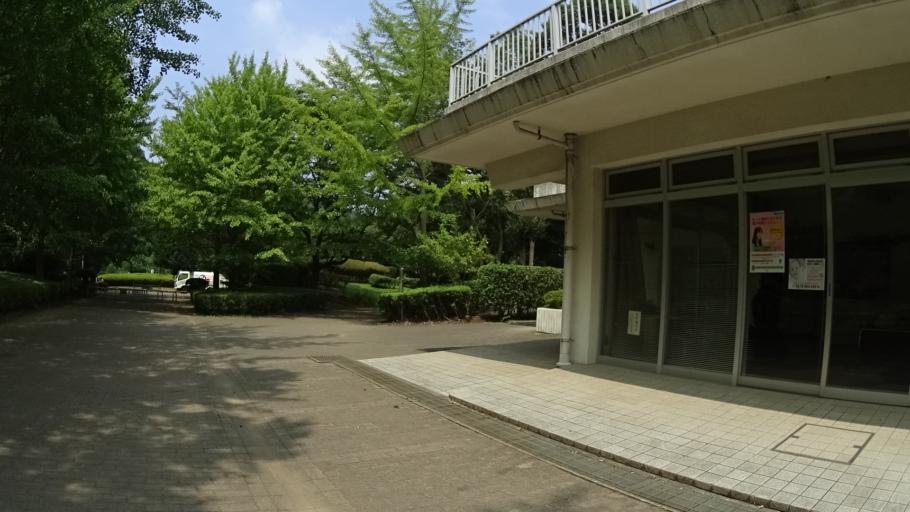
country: JP
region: Kanagawa
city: Hayama
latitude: 35.2845
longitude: 139.6014
